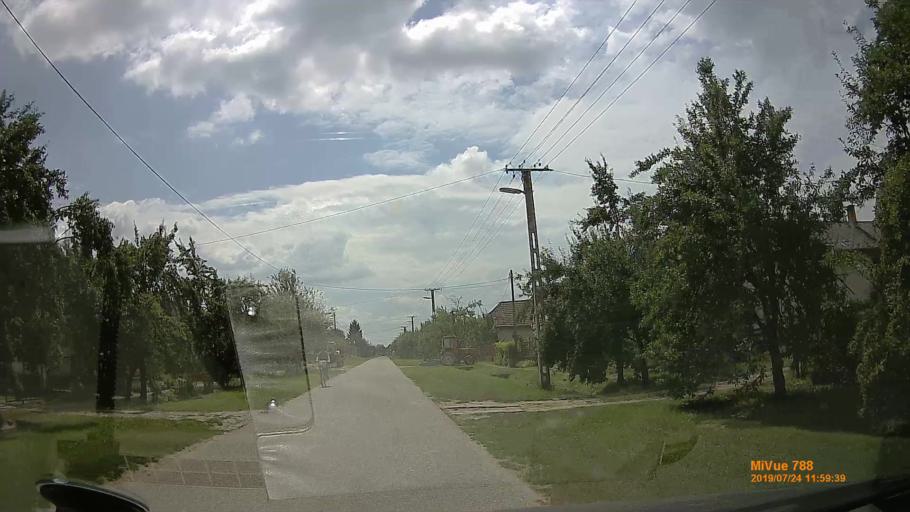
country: HU
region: Szabolcs-Szatmar-Bereg
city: Tarpa
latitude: 48.2015
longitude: 22.4510
